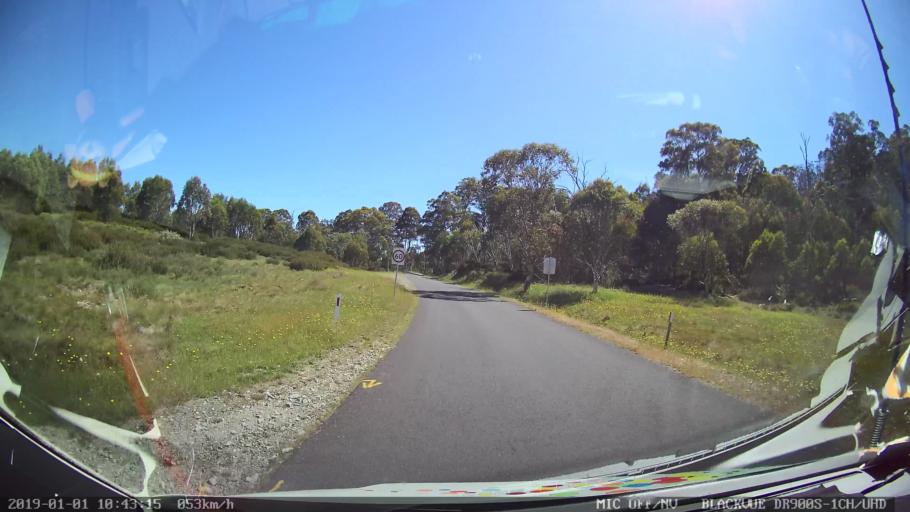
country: AU
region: New South Wales
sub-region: Snowy River
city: Jindabyne
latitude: -36.0371
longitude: 148.3236
